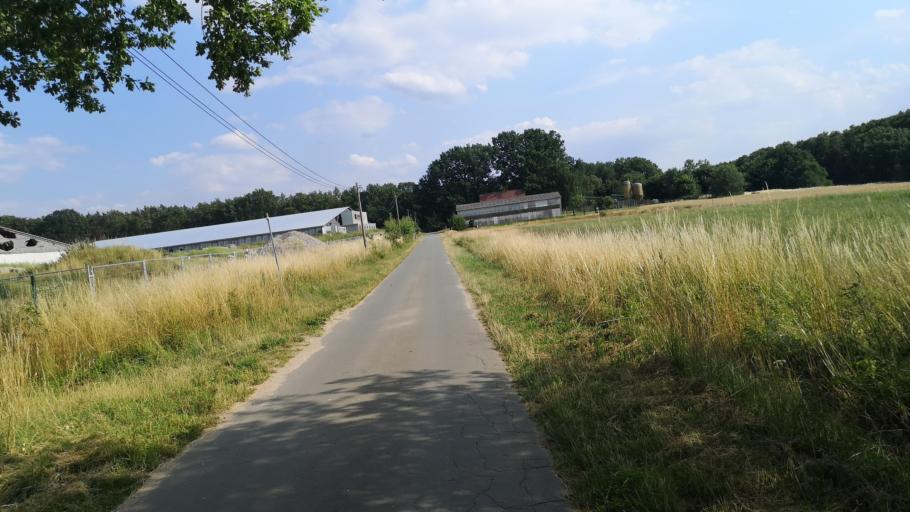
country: DE
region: Lower Saxony
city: Dahlenburg
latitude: 53.2186
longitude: 10.7121
